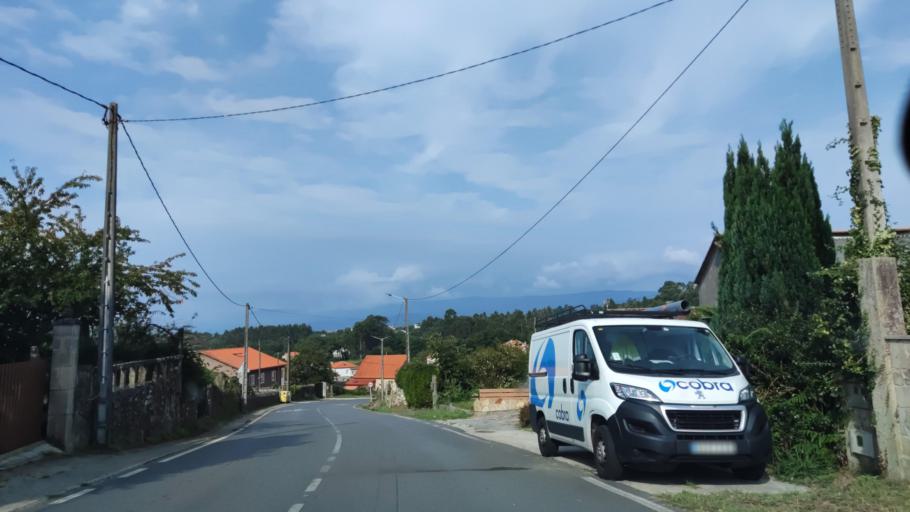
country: ES
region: Galicia
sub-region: Provincia da Coruna
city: Rianxo
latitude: 42.6478
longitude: -8.7931
